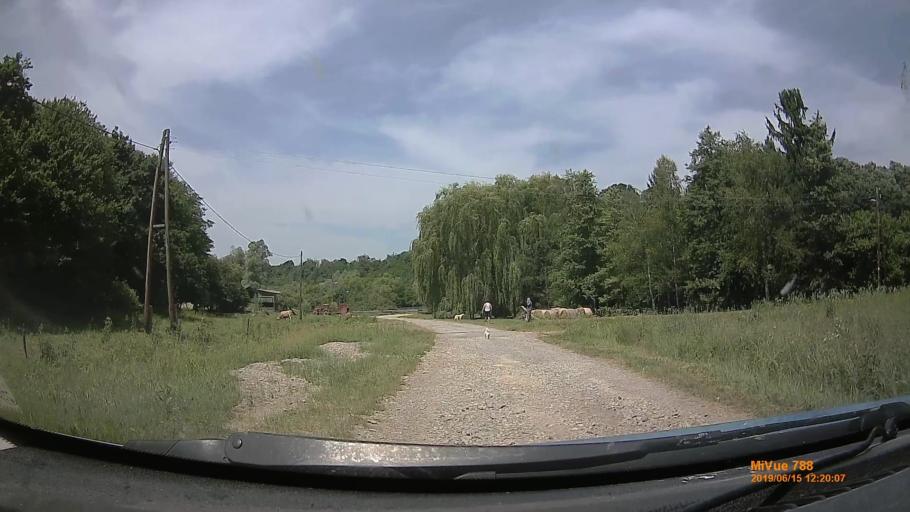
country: HU
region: Baranya
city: Buekkoesd
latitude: 46.1063
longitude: 18.0157
